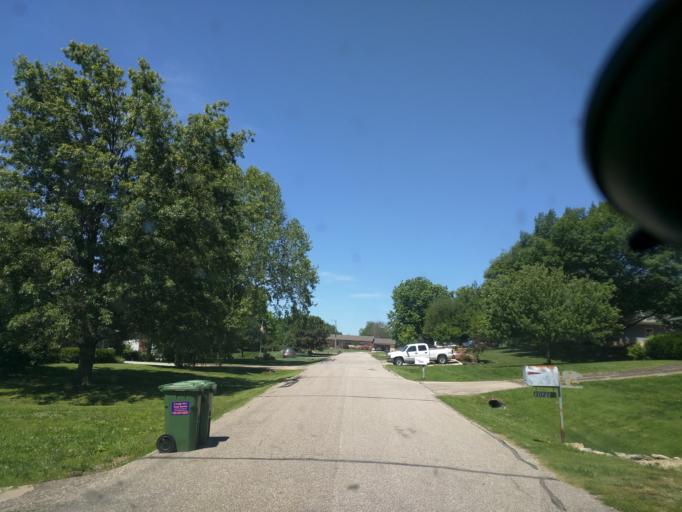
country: US
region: Kansas
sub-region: Riley County
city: Manhattan
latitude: 39.2162
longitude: -96.6143
